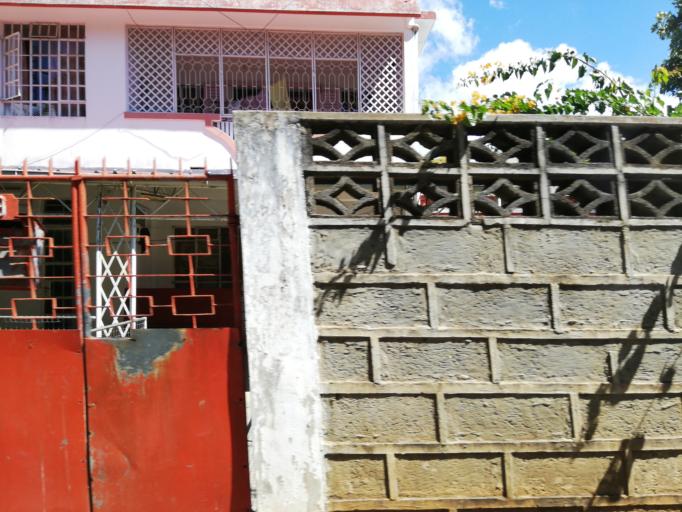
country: MU
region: Moka
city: Moka
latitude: -20.2269
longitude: 57.4648
